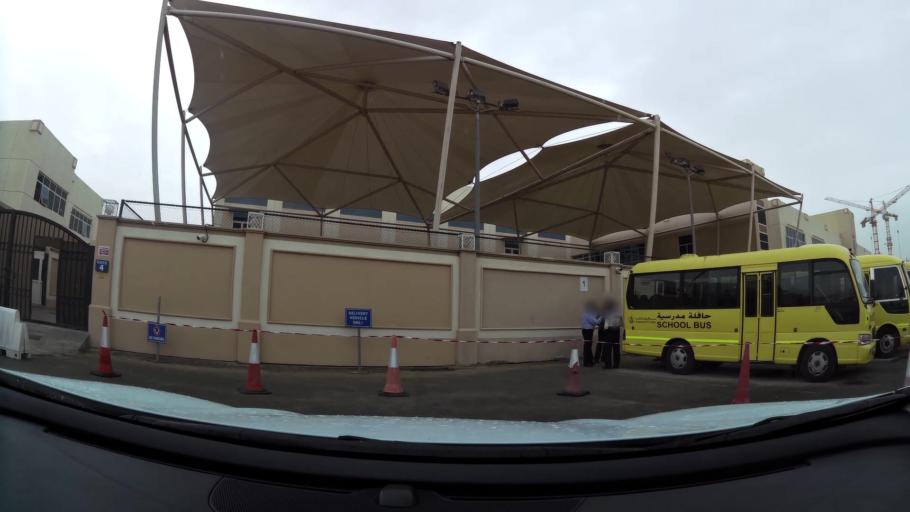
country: AE
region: Abu Dhabi
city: Abu Dhabi
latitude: 24.4291
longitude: 54.5849
